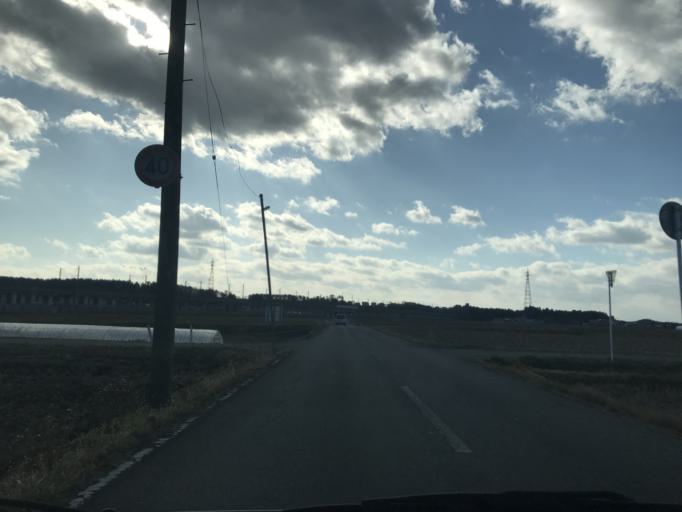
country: JP
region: Iwate
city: Ichinoseki
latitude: 38.7442
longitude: 141.0664
